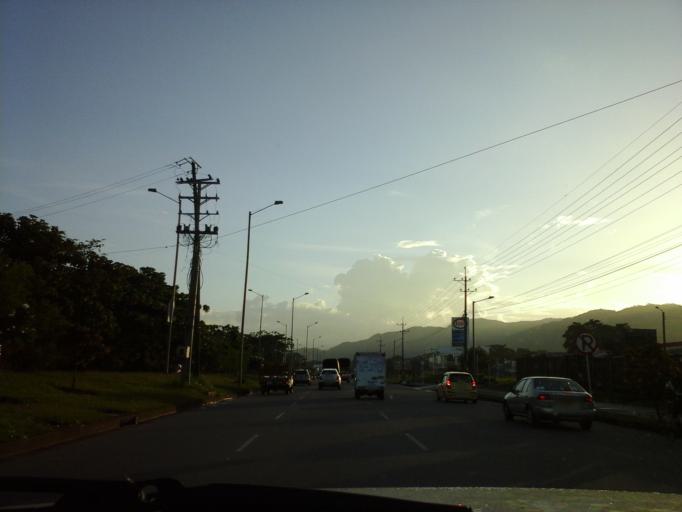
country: CO
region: Meta
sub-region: Villavicencio
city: Villavicencio
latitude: 4.1164
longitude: -73.6271
